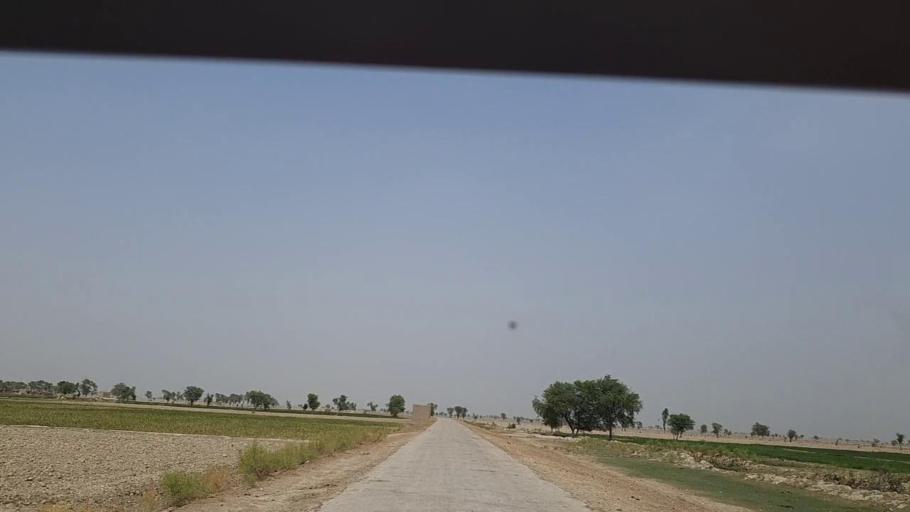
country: PK
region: Sindh
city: Khairpur Nathan Shah
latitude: 27.0260
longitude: 67.5960
